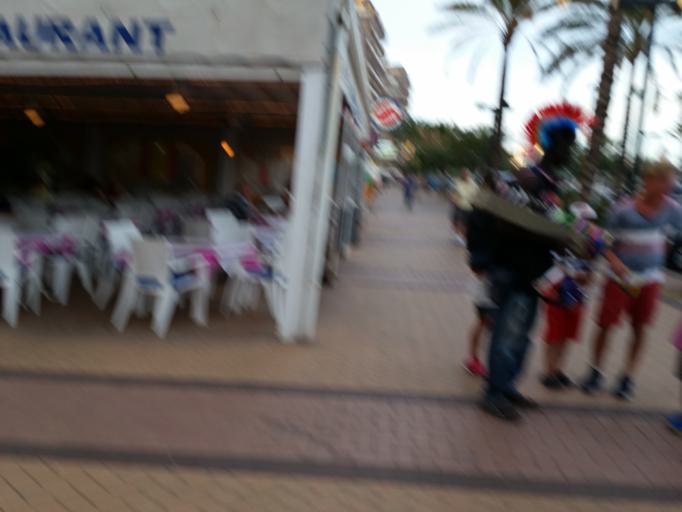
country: ES
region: Andalusia
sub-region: Provincia de Malaga
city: Fuengirola
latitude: 36.5589
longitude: -4.6090
